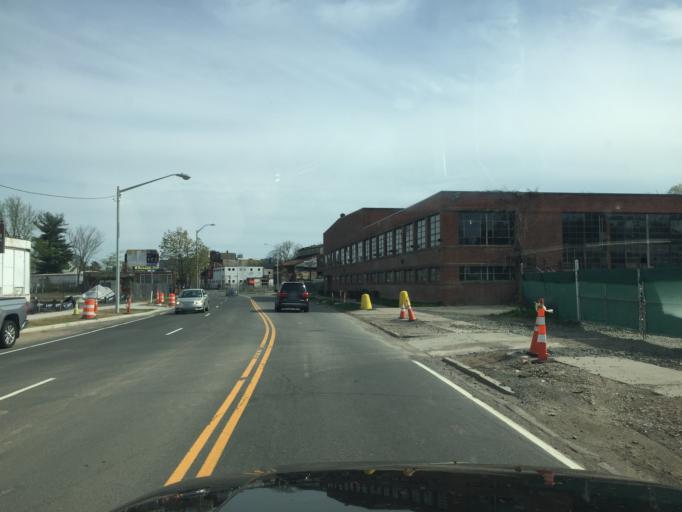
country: US
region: Connecticut
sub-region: Hartford County
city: Hartford
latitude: 41.7833
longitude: -72.7030
